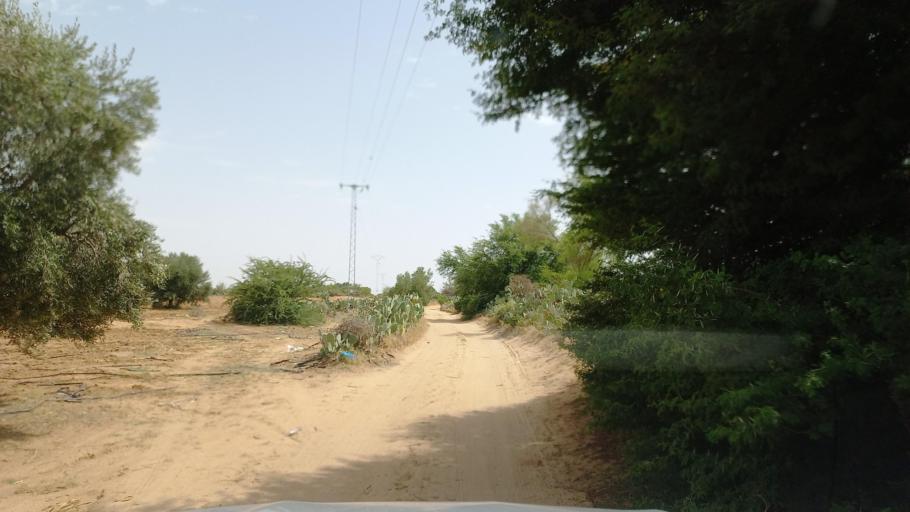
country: TN
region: Al Qasrayn
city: Kasserine
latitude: 35.2619
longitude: 9.0516
